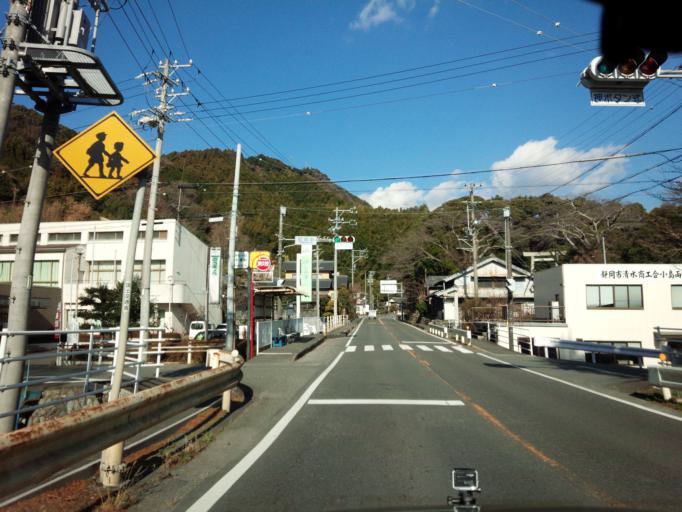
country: JP
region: Shizuoka
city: Fujinomiya
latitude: 35.1012
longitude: 138.5119
